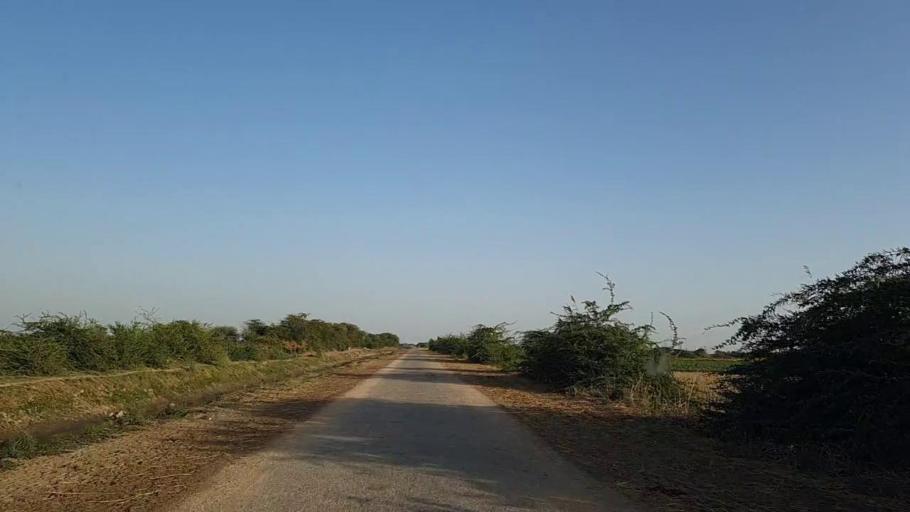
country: PK
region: Sindh
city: Jati
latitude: 24.4090
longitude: 68.3504
